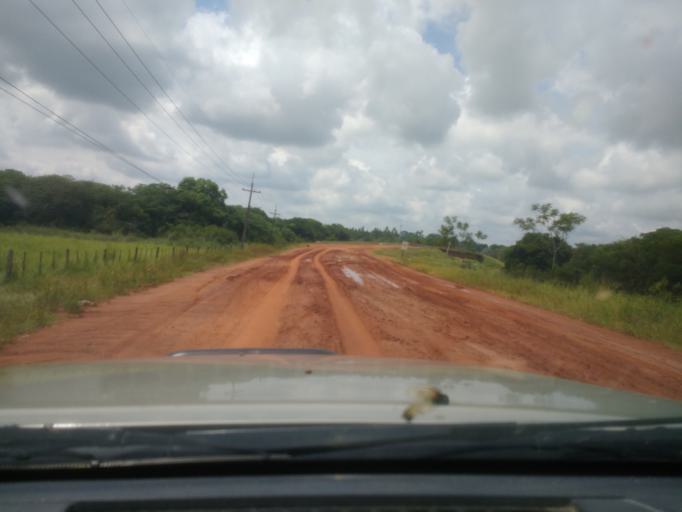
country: PY
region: San Pedro
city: Puerto Rosario
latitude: -24.4056
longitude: -57.1035
